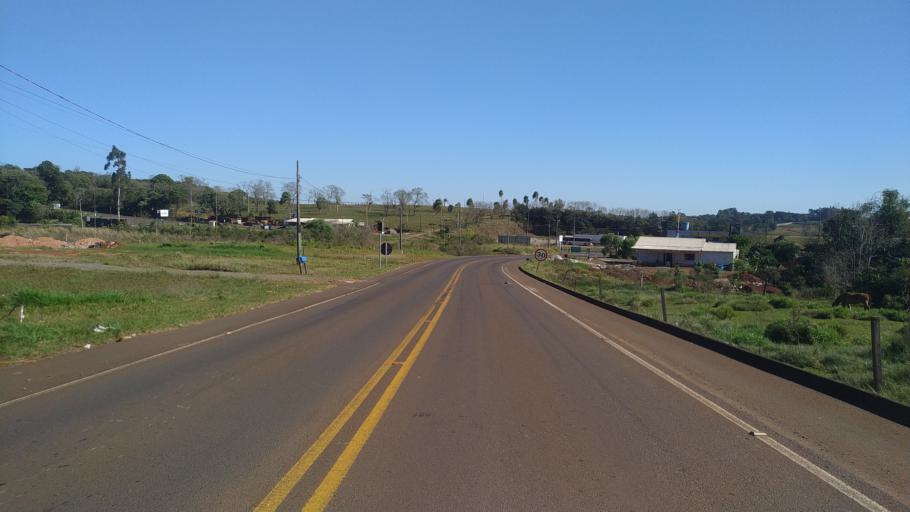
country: BR
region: Santa Catarina
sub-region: Chapeco
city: Chapeco
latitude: -27.1517
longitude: -52.6202
